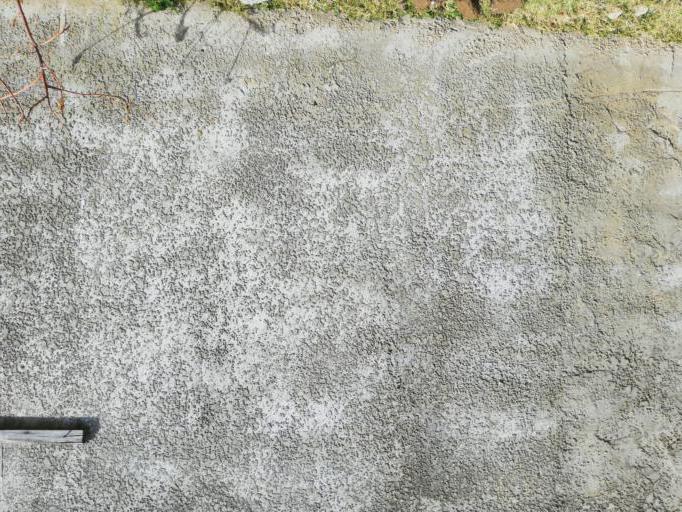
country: MU
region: Black River
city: Petite Riviere
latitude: -20.2244
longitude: 57.4580
